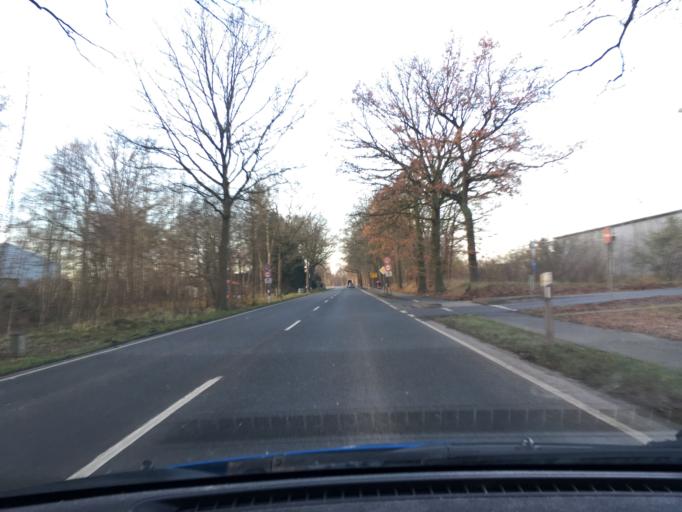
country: DE
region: Lower Saxony
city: Handorf
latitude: 53.3305
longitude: 10.3484
